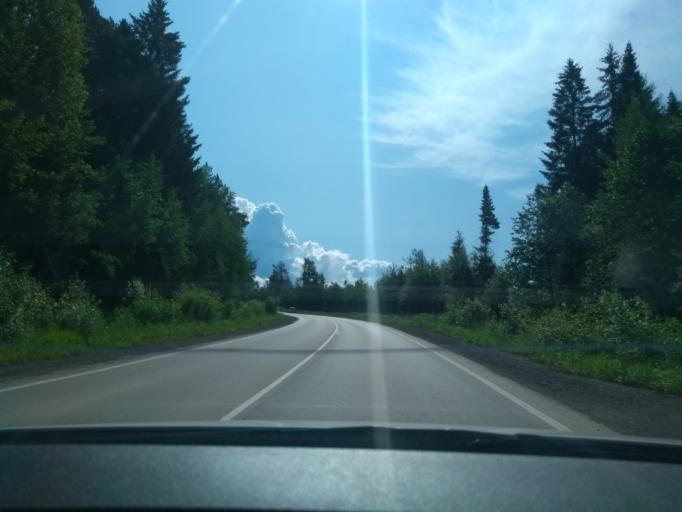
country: RU
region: Perm
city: Bershet'
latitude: 57.8263
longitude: 56.4168
